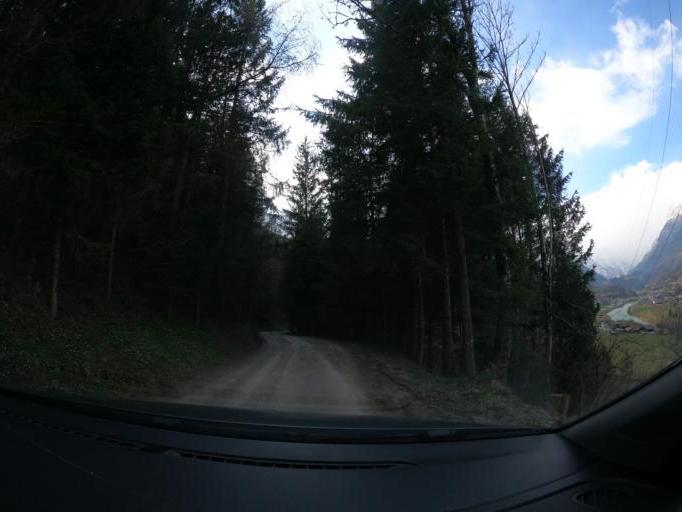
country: AT
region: Salzburg
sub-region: Politischer Bezirk Sankt Johann im Pongau
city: Pfarrwerfen
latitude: 47.4508
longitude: 13.2038
